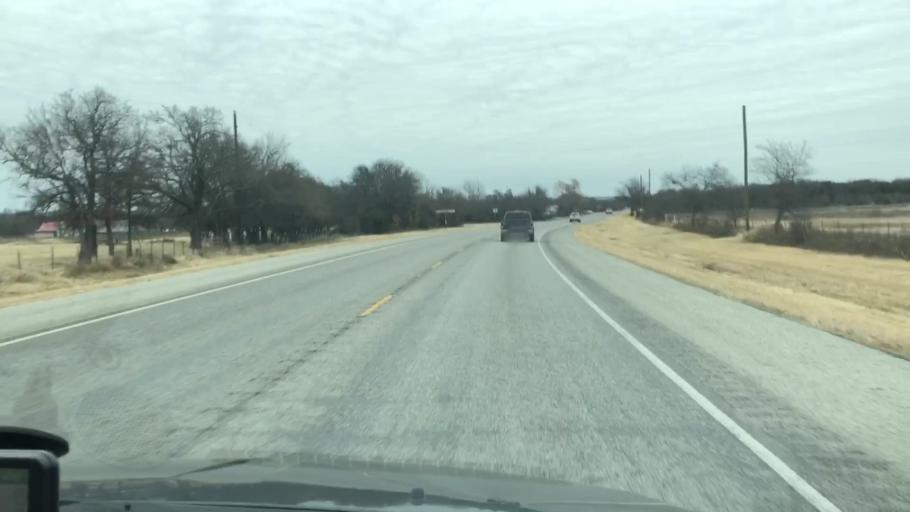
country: US
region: Texas
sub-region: Palo Pinto County
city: Mineral Wells
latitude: 32.8898
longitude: -98.0881
